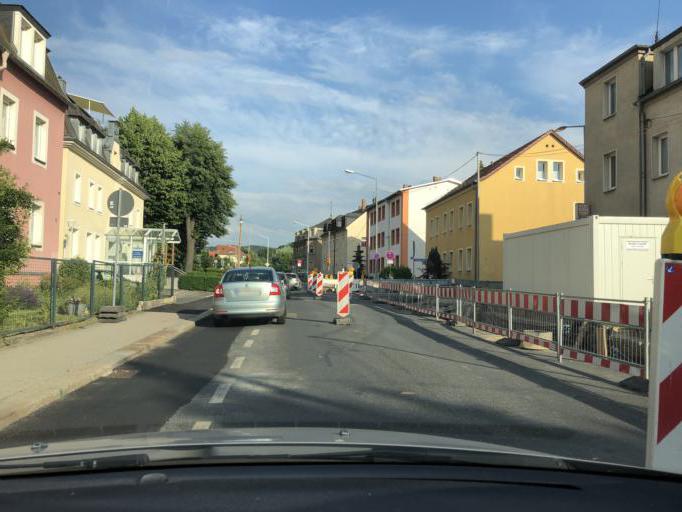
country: DE
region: Saxony
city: Freital
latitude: 50.9937
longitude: 13.6551
